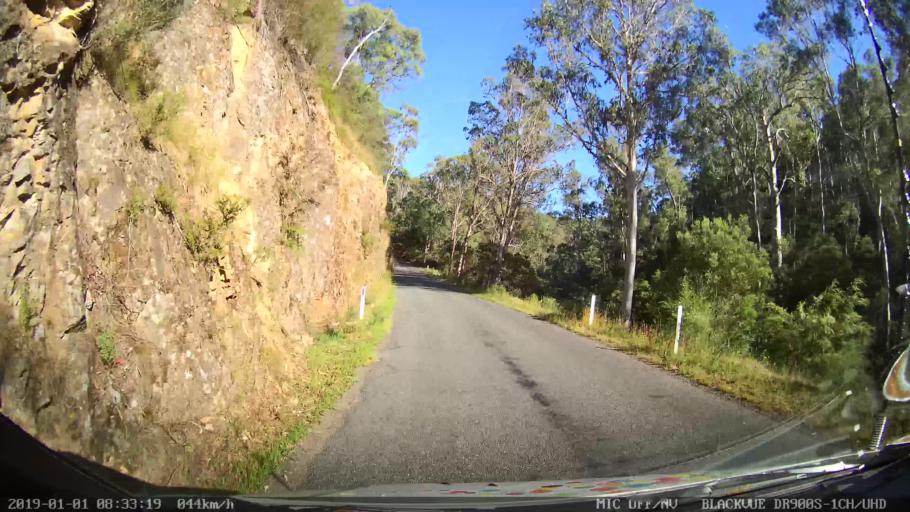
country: AU
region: New South Wales
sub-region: Snowy River
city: Jindabyne
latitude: -36.3557
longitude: 148.2030
